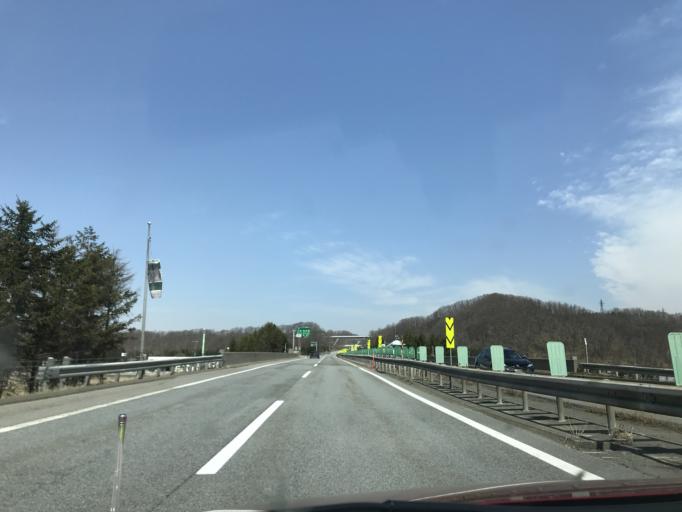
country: JP
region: Hokkaido
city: Iwamizawa
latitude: 43.2395
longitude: 141.8303
